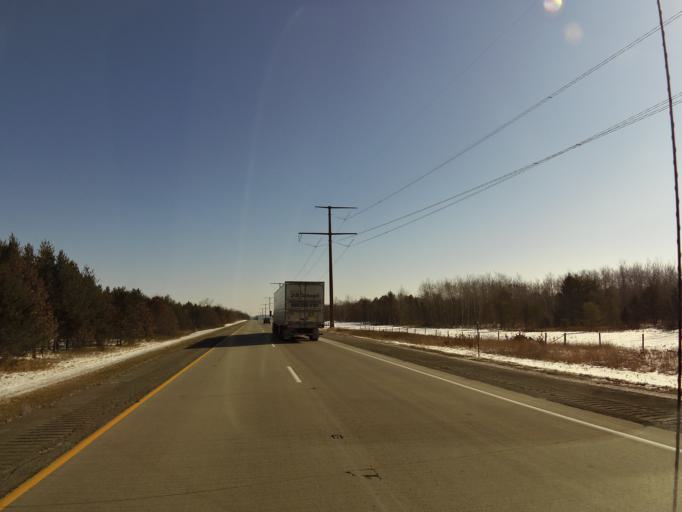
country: US
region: Wisconsin
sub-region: Columbia County
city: Wisconsin Dells
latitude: 43.7013
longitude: -89.8672
